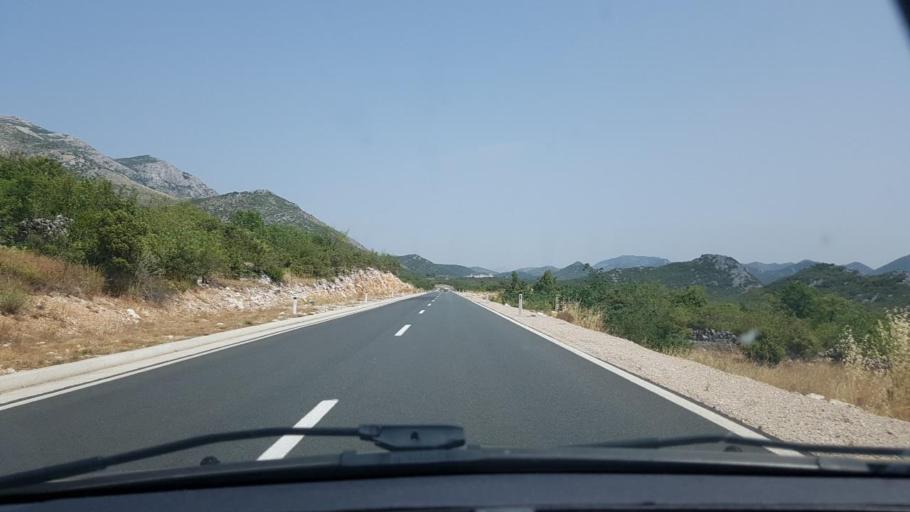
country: BA
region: Federation of Bosnia and Herzegovina
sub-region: Hercegovacko-Bosanski Kanton
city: Neum
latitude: 42.9604
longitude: 17.7065
